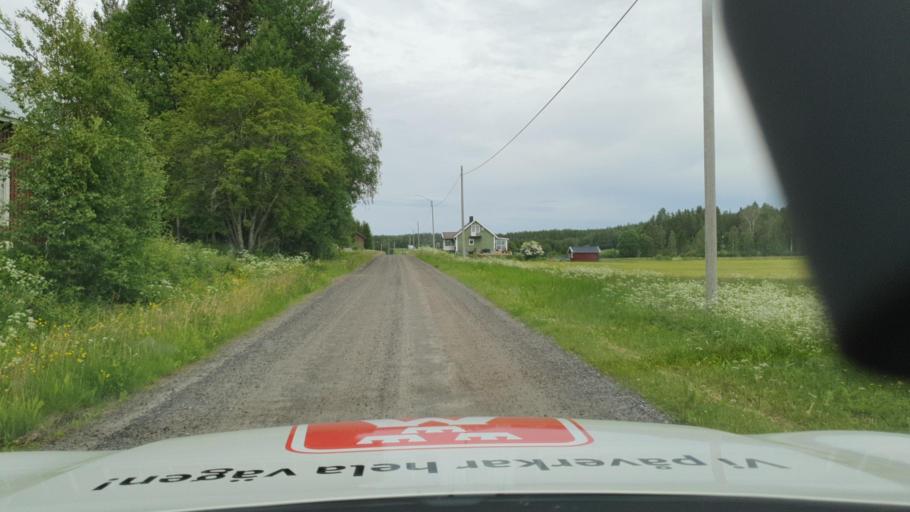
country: SE
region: Vaesterbotten
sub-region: Robertsfors Kommun
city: Robertsfors
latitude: 64.1829
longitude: 20.7334
